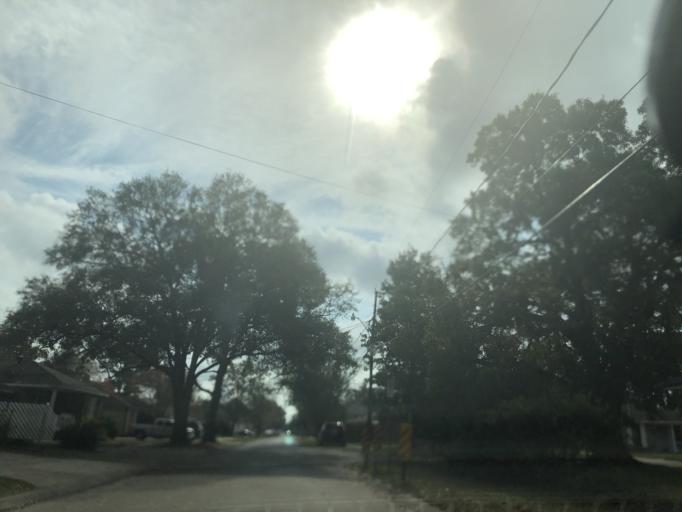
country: US
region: Louisiana
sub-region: Jefferson Parish
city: Metairie
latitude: 29.9889
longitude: -90.1589
